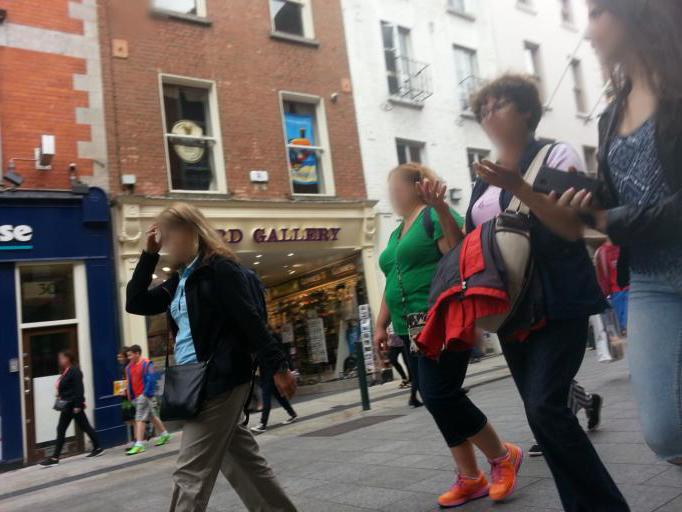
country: IE
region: Leinster
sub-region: Dublin City
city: Dublin
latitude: 53.3415
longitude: -6.2603
